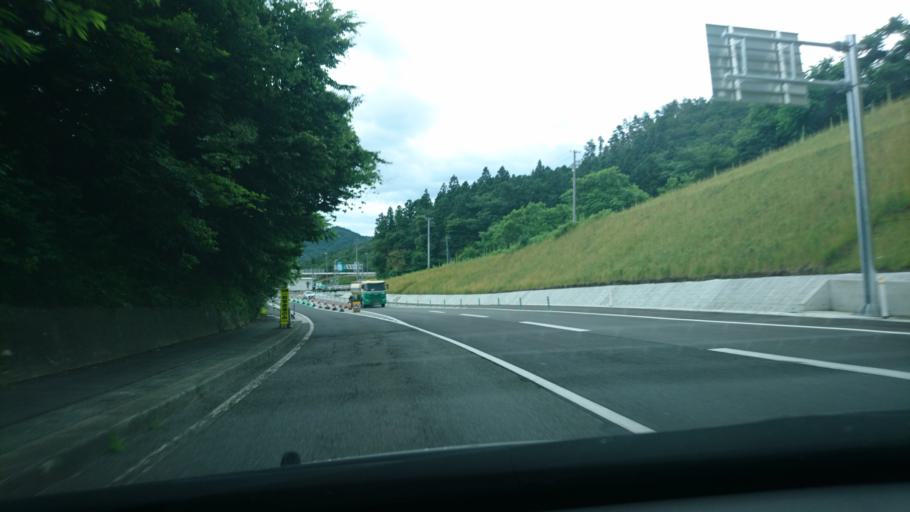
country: JP
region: Iwate
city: Kamaishi
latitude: 39.1912
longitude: 141.8480
